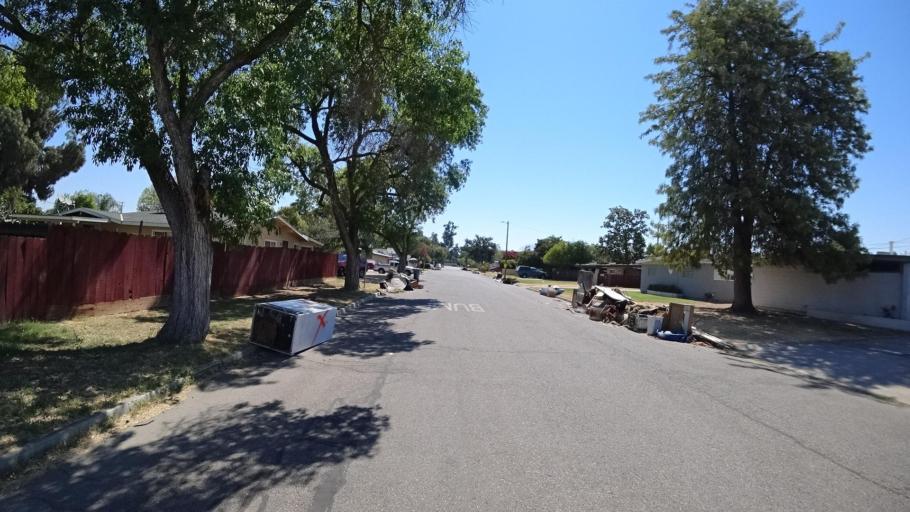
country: US
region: California
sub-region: Fresno County
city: Fresno
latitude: 36.7890
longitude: -119.7799
